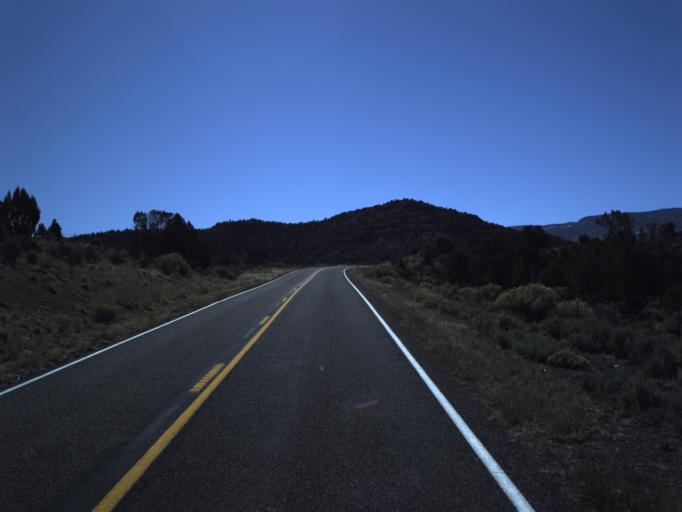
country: US
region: Utah
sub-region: Wayne County
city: Loa
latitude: 38.2677
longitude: -111.3750
